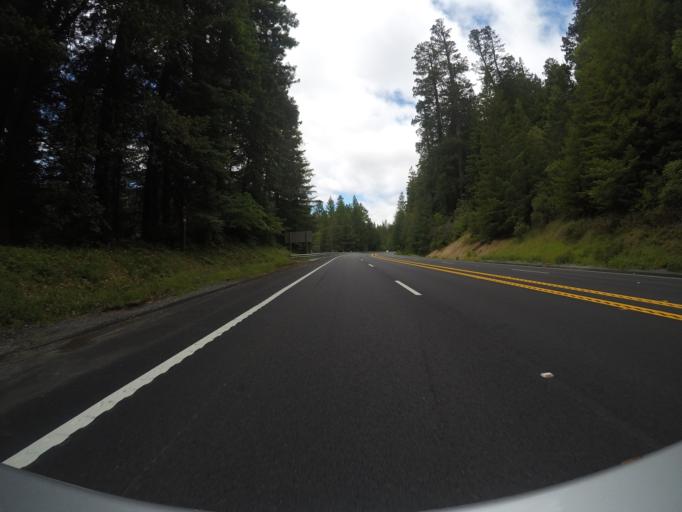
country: US
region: California
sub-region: Humboldt County
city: Redway
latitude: 40.3140
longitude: -123.9141
